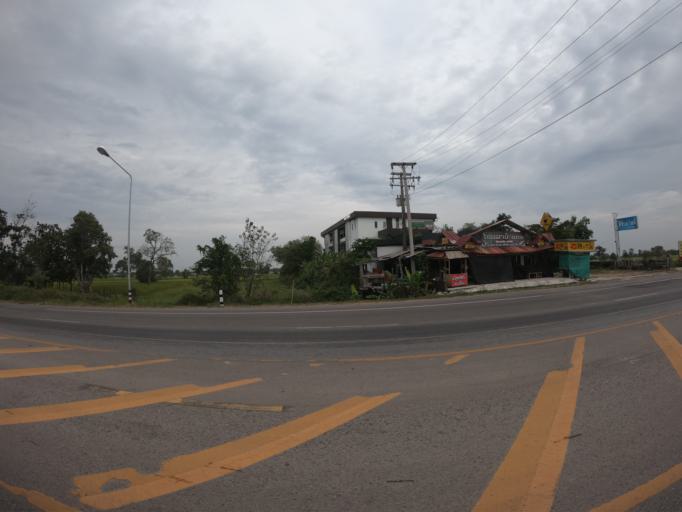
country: TH
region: Roi Et
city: Chiang Khwan
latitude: 16.1400
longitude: 103.8568
